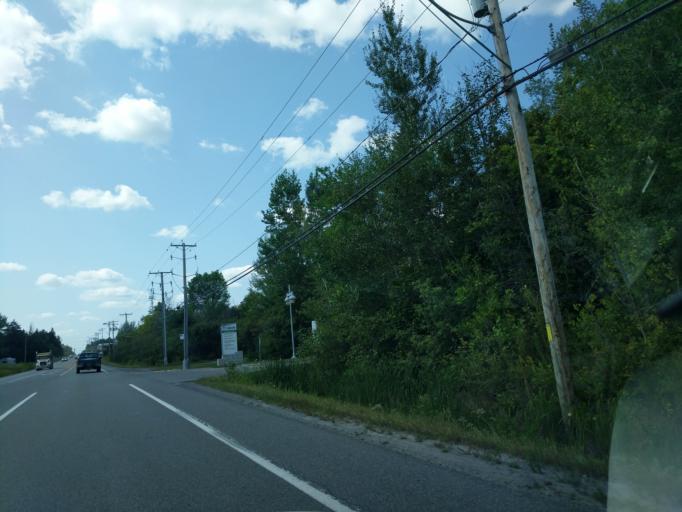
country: CA
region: Quebec
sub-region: Outaouais
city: Gatineau
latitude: 45.4424
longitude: -75.8103
